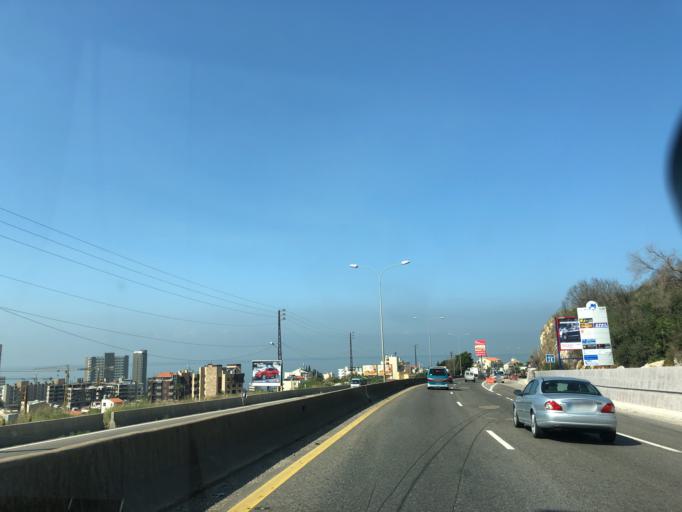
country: LB
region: Mont-Liban
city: Djounie
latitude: 34.0174
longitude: 35.6363
